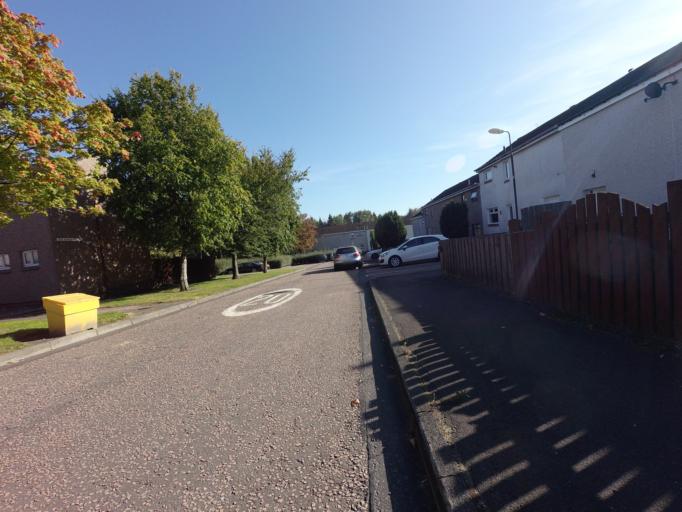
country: GB
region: Scotland
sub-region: West Lothian
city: Livingston
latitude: 55.8989
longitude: -3.5574
